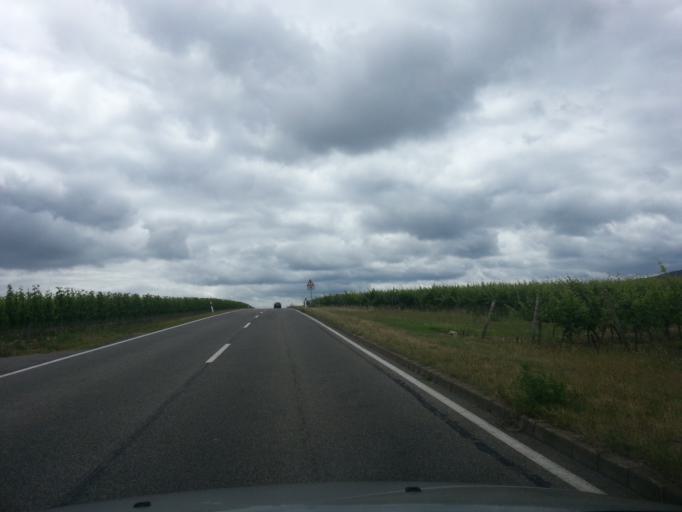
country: DE
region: Rheinland-Pfalz
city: Weisenheim am Berg
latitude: 49.5063
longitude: 8.1584
